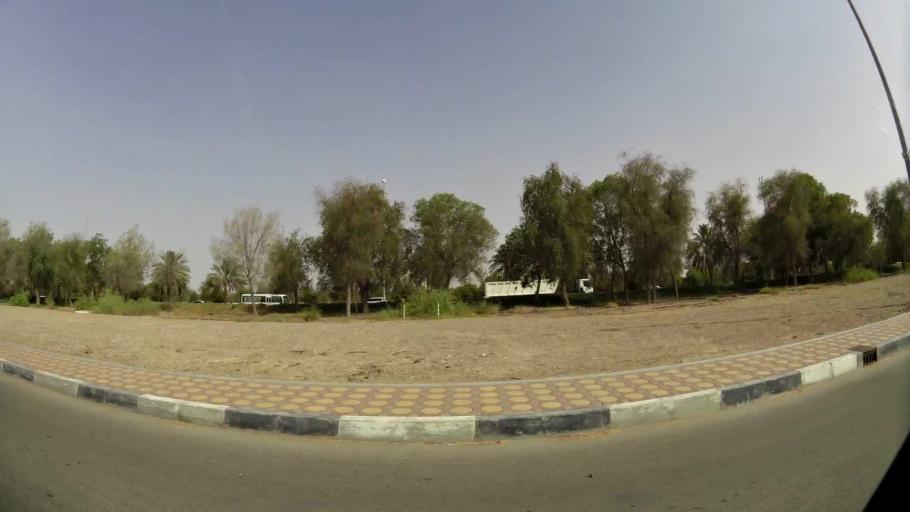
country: AE
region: Abu Dhabi
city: Al Ain
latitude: 24.1803
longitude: 55.6215
